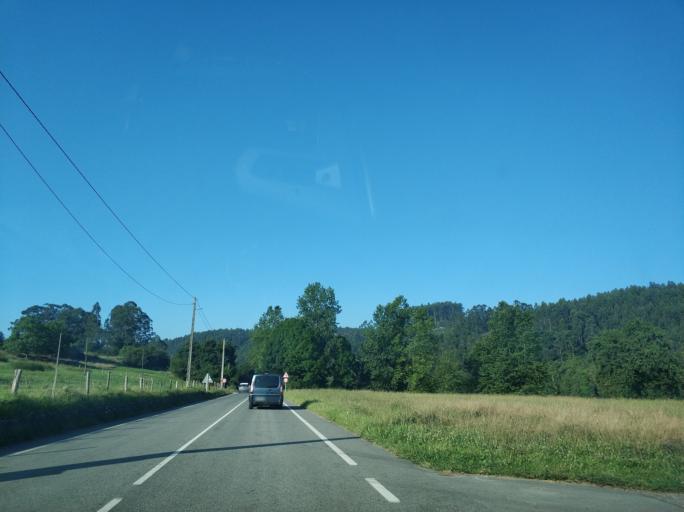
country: ES
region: Cantabria
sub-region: Provincia de Cantabria
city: Polanco
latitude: 43.3851
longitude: -3.9673
